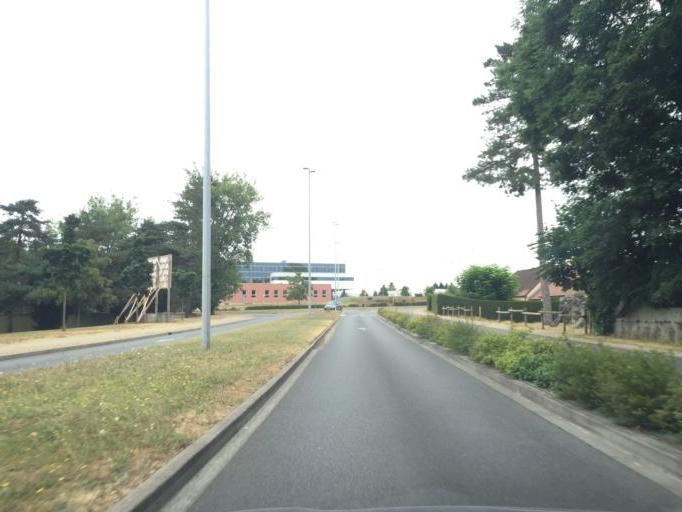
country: FR
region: Auvergne
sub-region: Departement de l'Allier
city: Moulins
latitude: 46.5398
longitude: 3.3364
